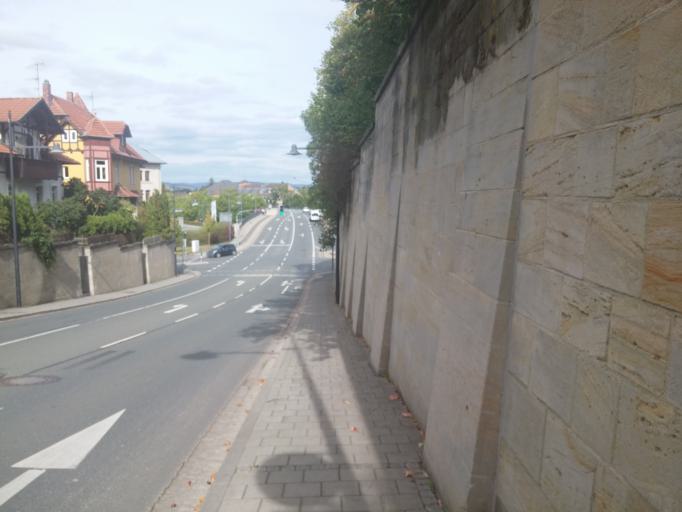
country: DE
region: Bavaria
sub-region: Upper Franconia
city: Coburg
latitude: 50.2523
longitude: 10.9573
